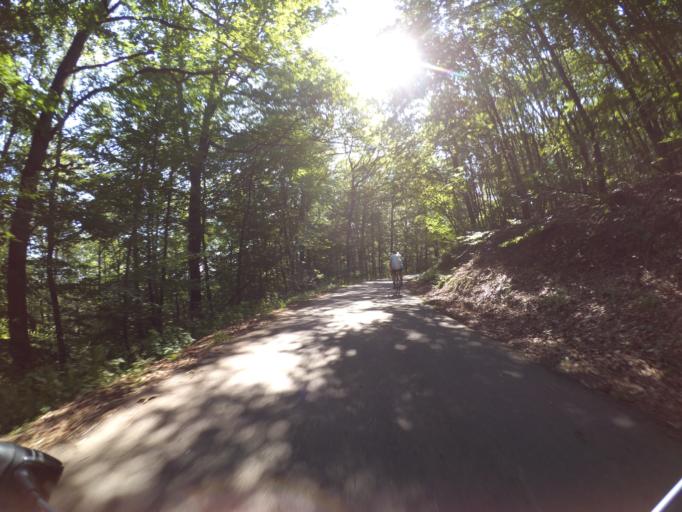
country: DE
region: Rheinland-Pfalz
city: Immert
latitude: 49.7699
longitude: 7.0098
